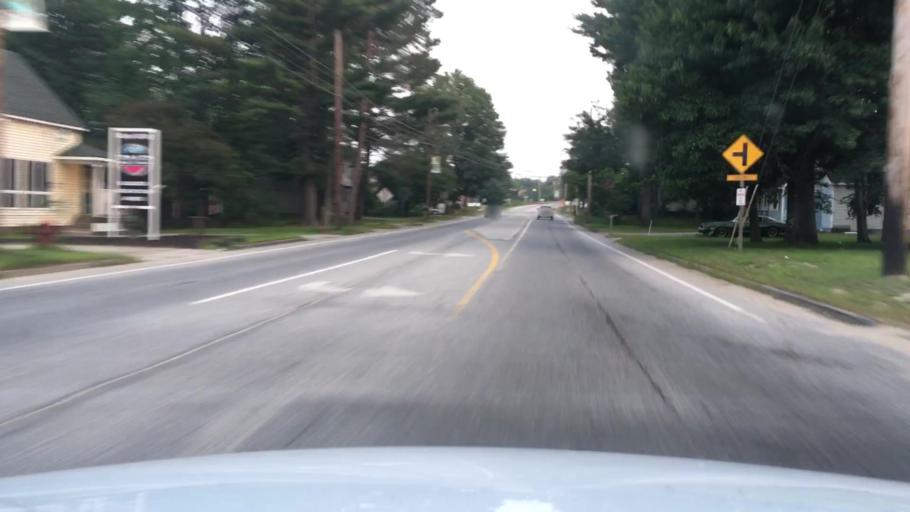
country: US
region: Maine
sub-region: Oxford County
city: Bethel
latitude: 44.4142
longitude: -70.7963
